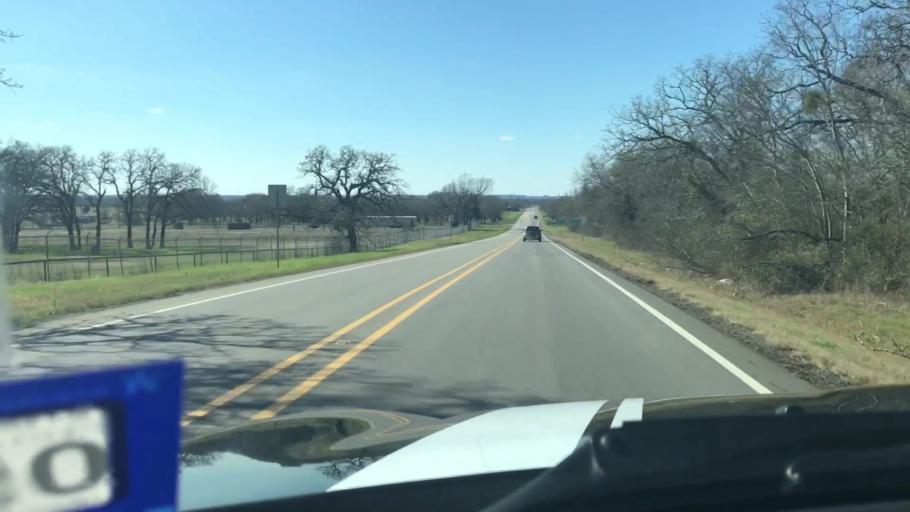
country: US
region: Texas
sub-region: Robertson County
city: Hearne
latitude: 30.8900
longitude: -96.6172
